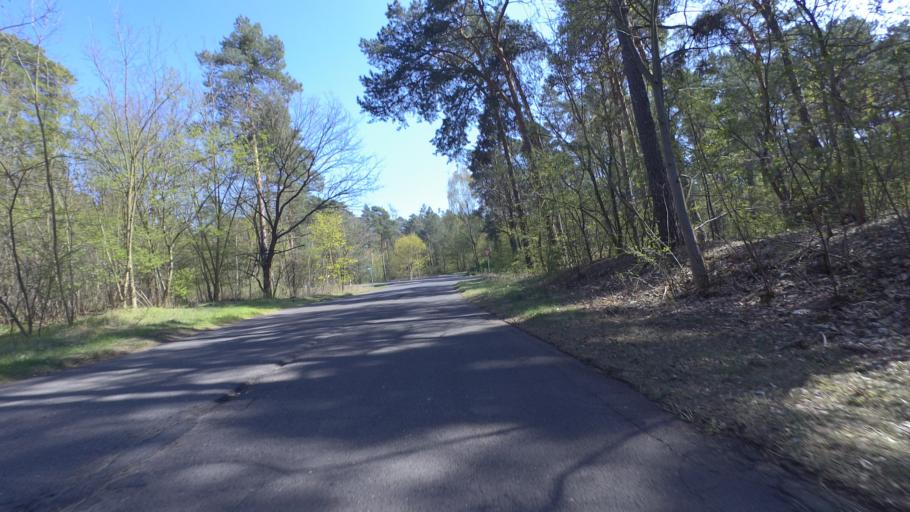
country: DE
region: Brandenburg
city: Zossen
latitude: 52.1664
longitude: 13.4890
